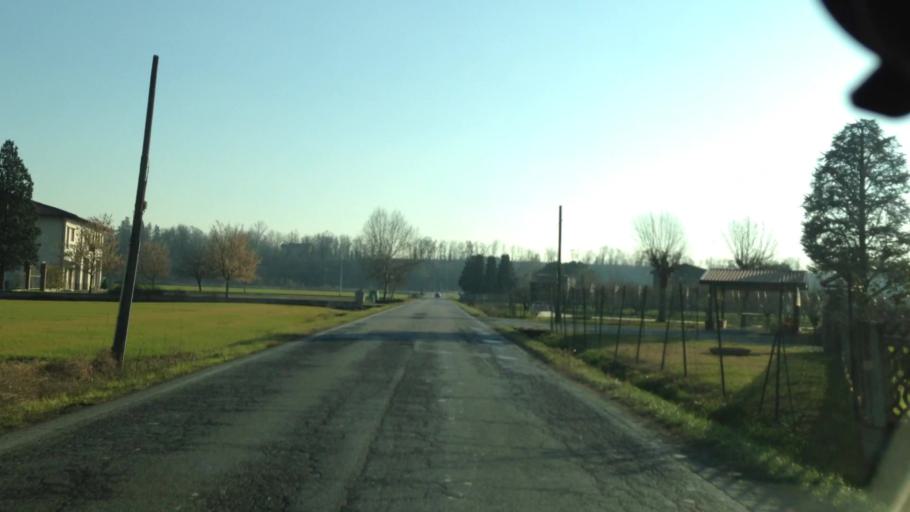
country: IT
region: Piedmont
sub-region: Provincia di Alessandria
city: Felizzano
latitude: 44.8775
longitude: 8.4444
